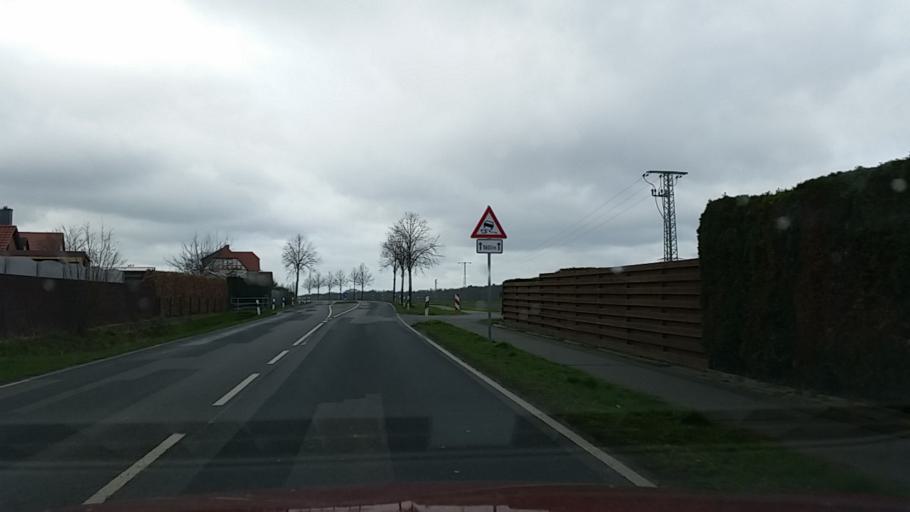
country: DE
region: Lower Saxony
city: Danndorf
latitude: 52.4252
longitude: 10.9087
